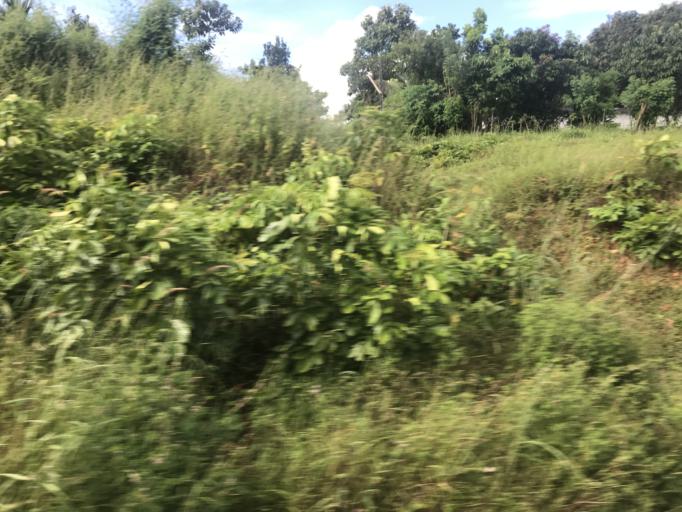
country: IN
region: Kerala
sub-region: Palakkad district
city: Palakkad
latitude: 10.8158
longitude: 76.6818
